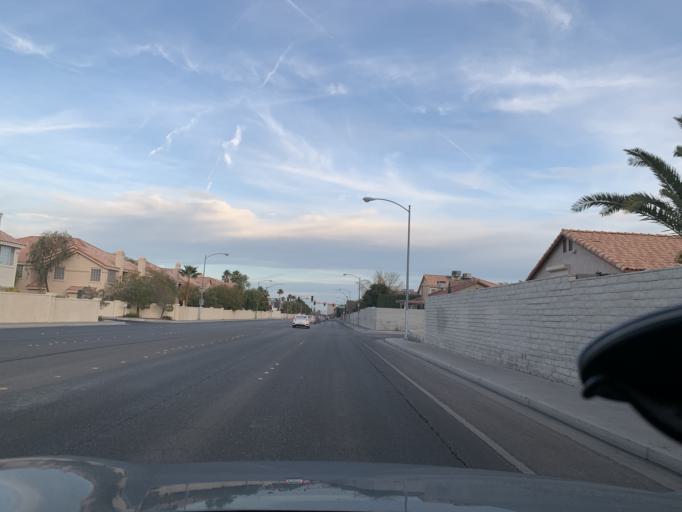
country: US
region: Nevada
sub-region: Clark County
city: Spring Valley
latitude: 36.0925
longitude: -115.2360
